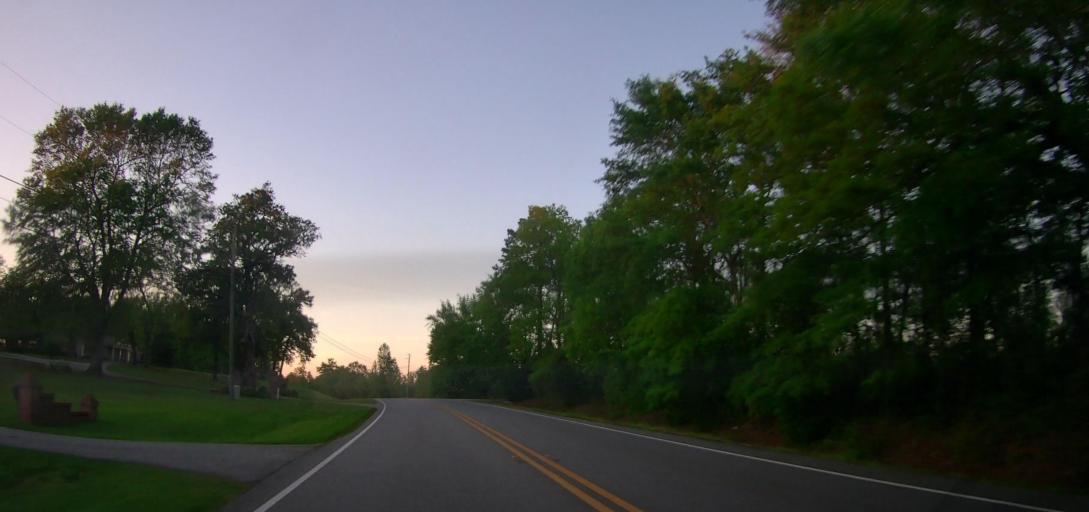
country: US
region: Georgia
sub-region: Marion County
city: Buena Vista
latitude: 32.3465
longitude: -84.5323
